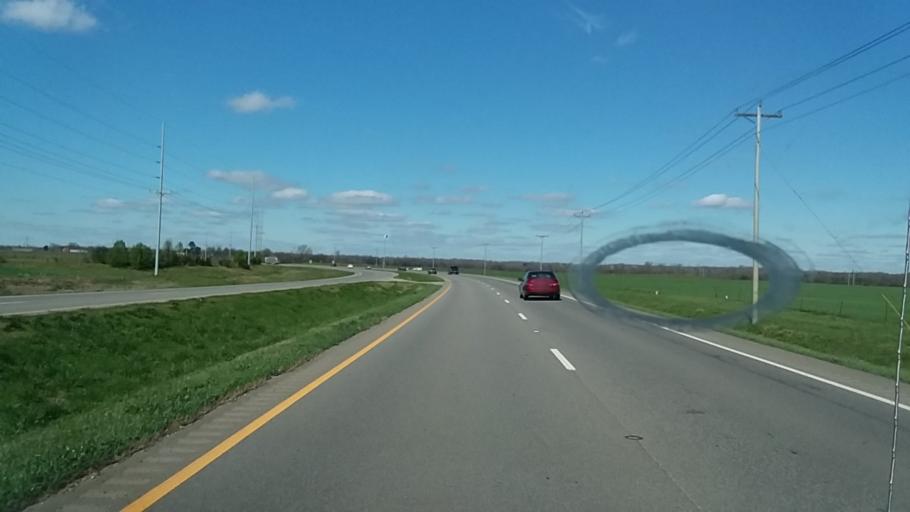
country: US
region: Alabama
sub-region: Morgan County
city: Trinity
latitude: 34.6334
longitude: -87.1011
